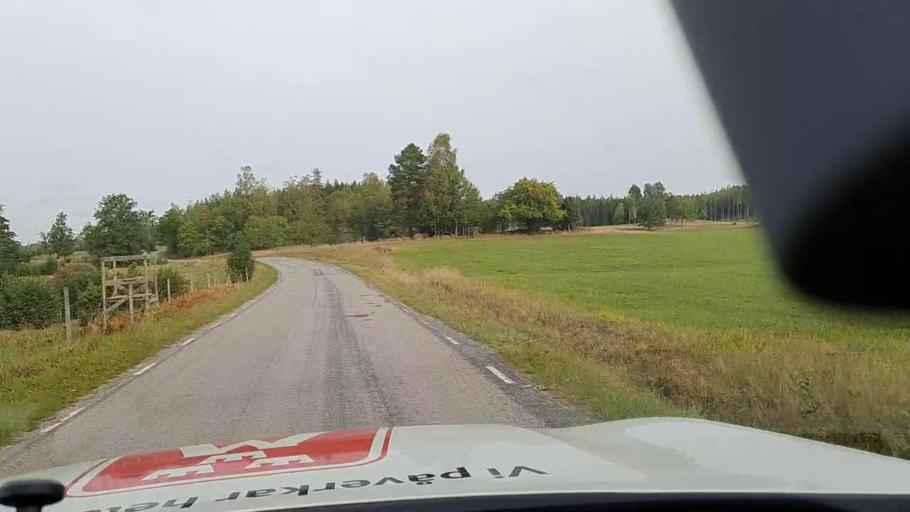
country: SE
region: Soedermanland
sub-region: Nykopings Kommun
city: Stigtomta
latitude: 58.9705
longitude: 16.9011
